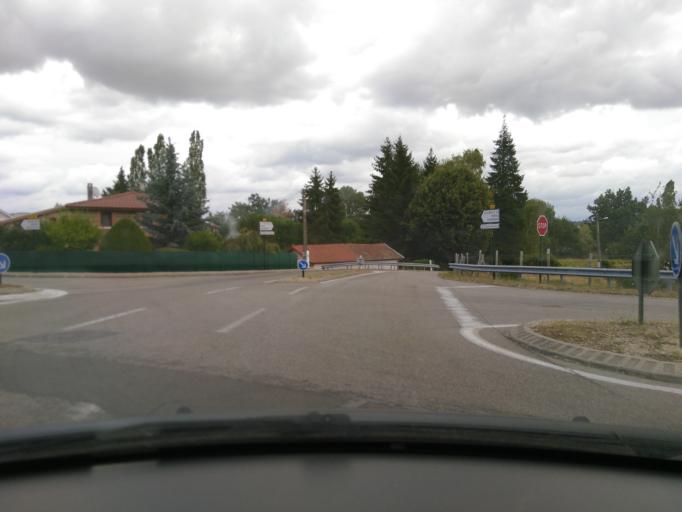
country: FR
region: Rhone-Alpes
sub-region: Departement de l'Isere
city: Saint-Jean-de-Bournay
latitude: 45.4029
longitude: 5.1295
